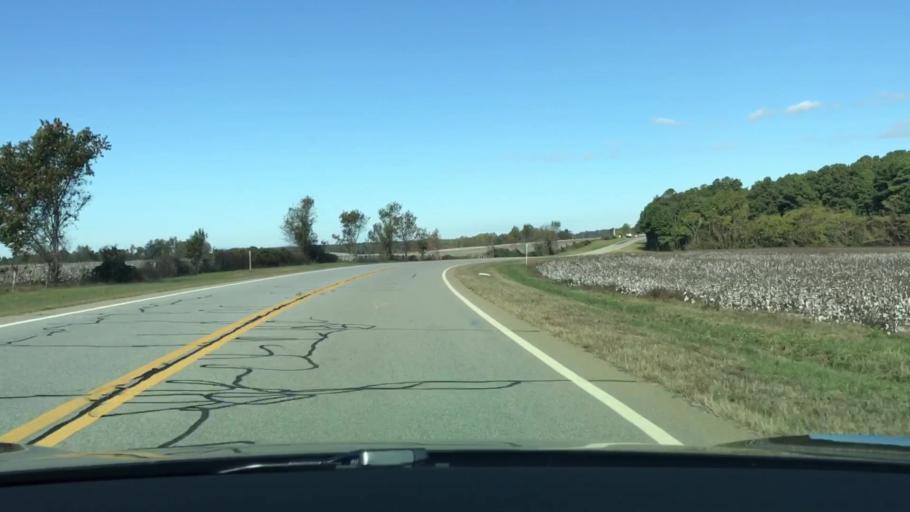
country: US
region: Georgia
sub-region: Warren County
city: Warrenton
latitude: 33.3569
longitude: -82.5944
